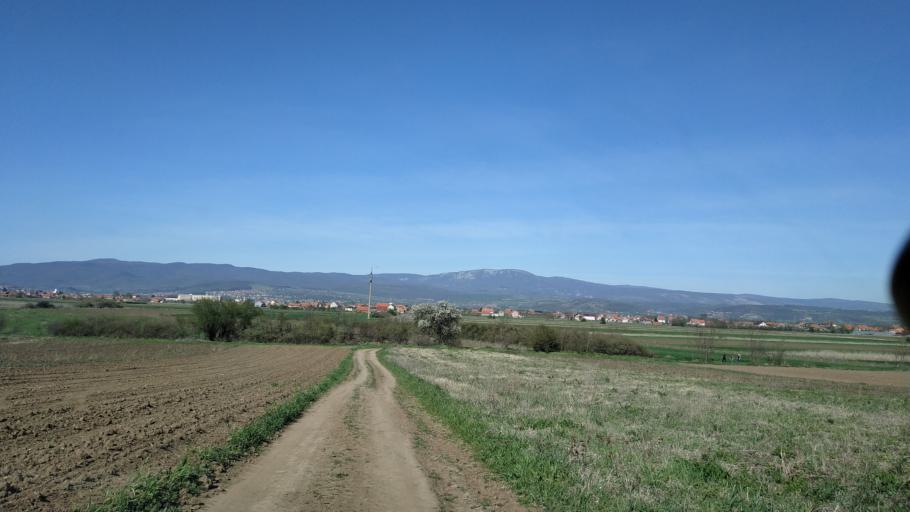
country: RS
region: Central Serbia
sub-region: Nisavski Okrug
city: Aleksinac
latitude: 43.4918
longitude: 21.6881
